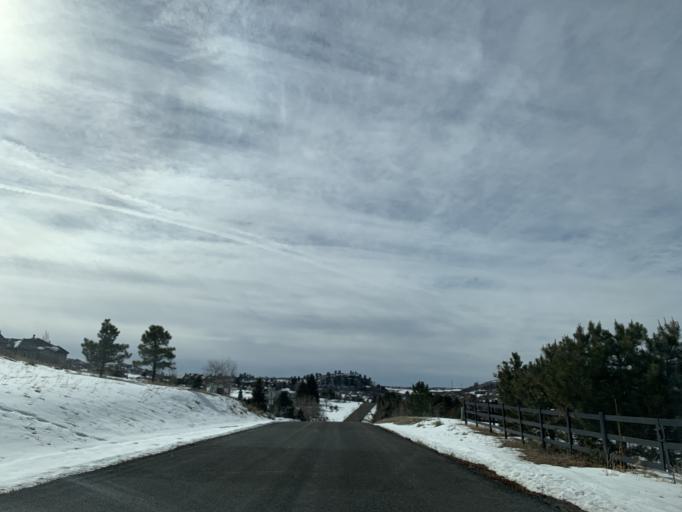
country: US
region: Colorado
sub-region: Douglas County
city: Carriage Club
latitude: 39.5186
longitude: -104.8989
